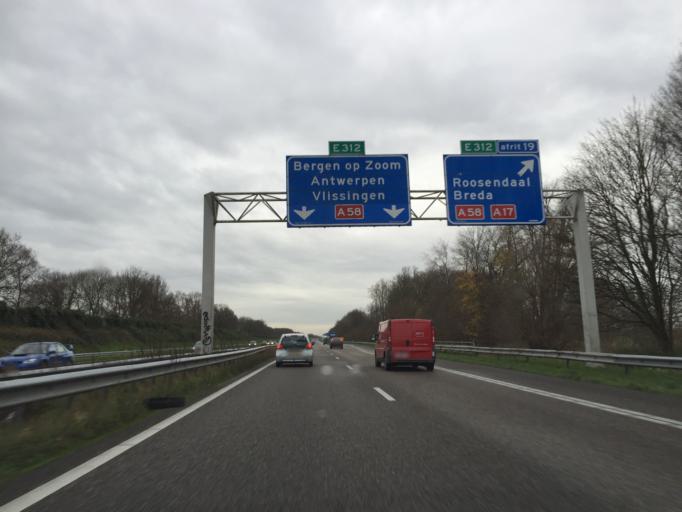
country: NL
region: North Brabant
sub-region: Roosendaal
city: Roosendaal
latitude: 51.5416
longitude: 4.4404
